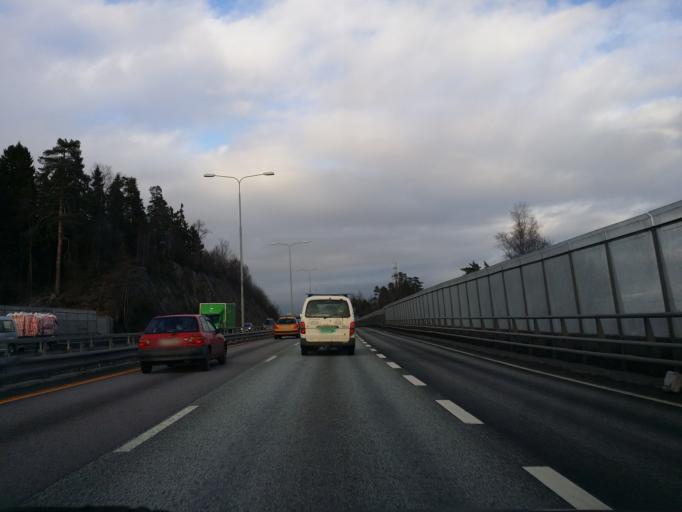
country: NO
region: Akershus
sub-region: Baerum
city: Sandvika
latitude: 59.8786
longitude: 10.5073
